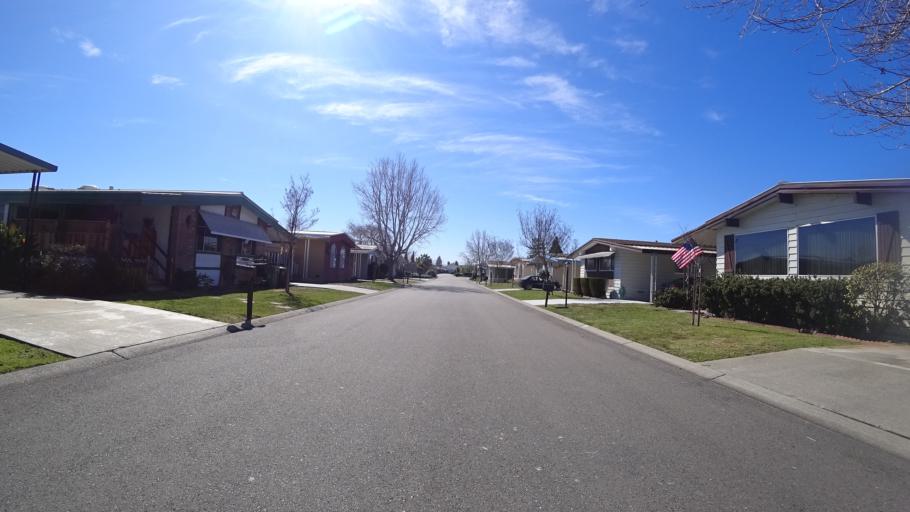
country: US
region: California
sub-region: Alameda County
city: Hayward
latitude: 37.6232
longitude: -122.0977
